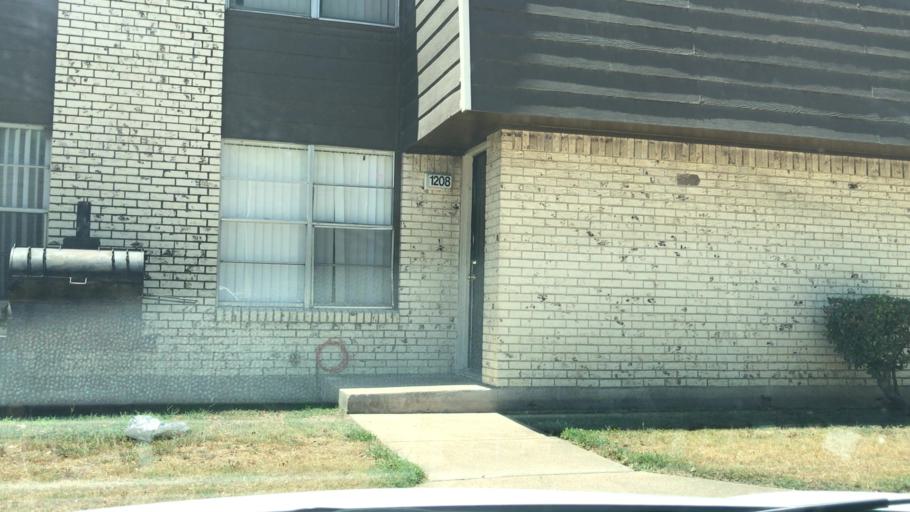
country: US
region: Texas
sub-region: Dallas County
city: Farmers Branch
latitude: 32.8932
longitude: -96.9097
